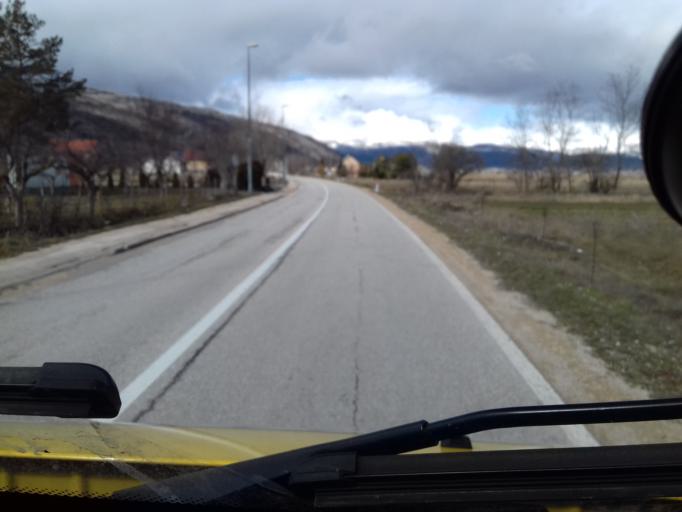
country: BA
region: Federation of Bosnia and Herzegovina
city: Tomislavgrad
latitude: 43.6495
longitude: 17.2264
